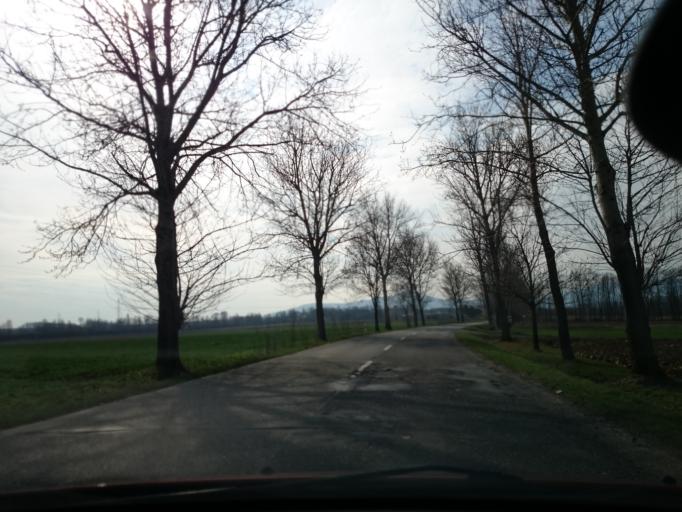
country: PL
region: Opole Voivodeship
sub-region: Powiat nyski
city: Glucholazy
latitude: 50.3404
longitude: 17.3888
